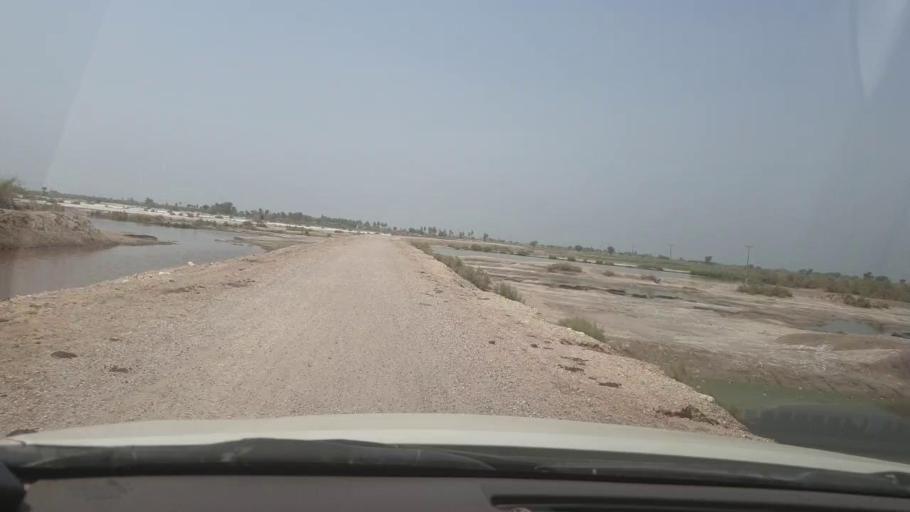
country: PK
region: Sindh
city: Garhi Yasin
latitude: 27.9727
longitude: 68.5491
